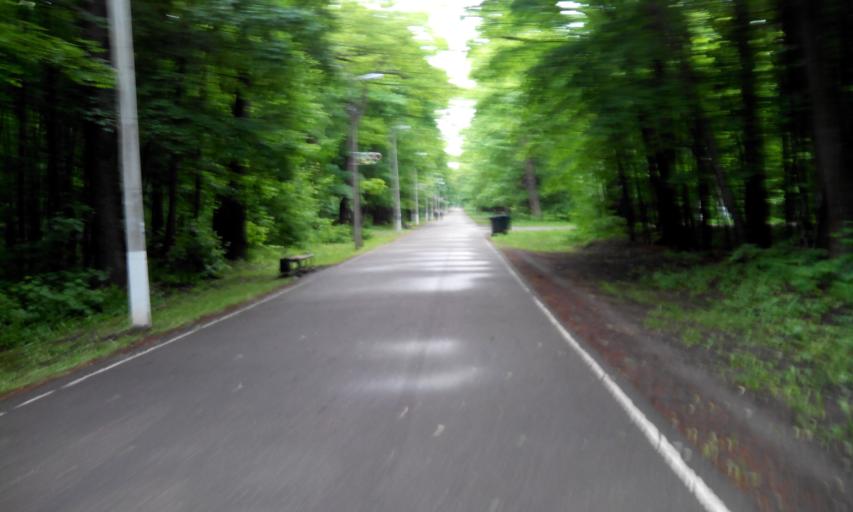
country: RU
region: Penza
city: Penza
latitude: 53.1804
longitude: 44.9674
